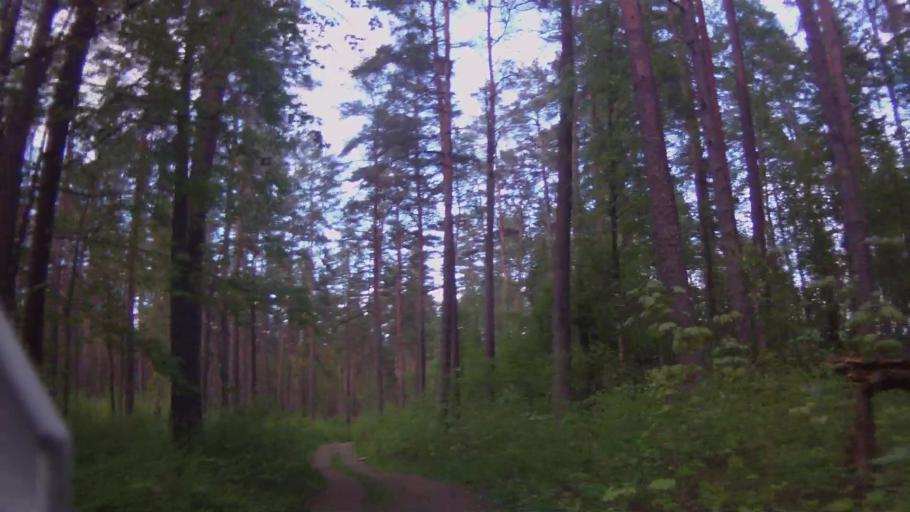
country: LV
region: Stopini
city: Ulbroka
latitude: 56.9618
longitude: 24.2703
